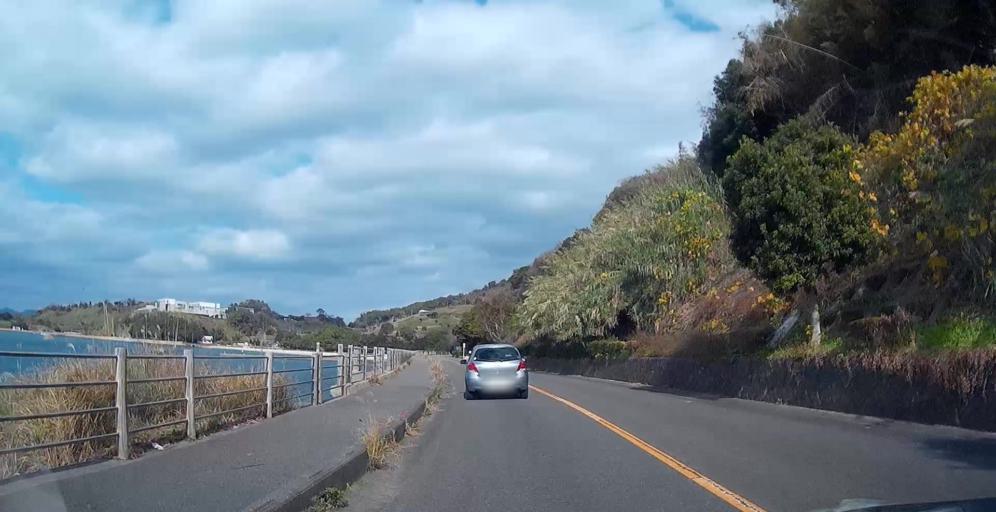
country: JP
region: Kumamoto
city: Minamata
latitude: 32.3149
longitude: 130.4711
